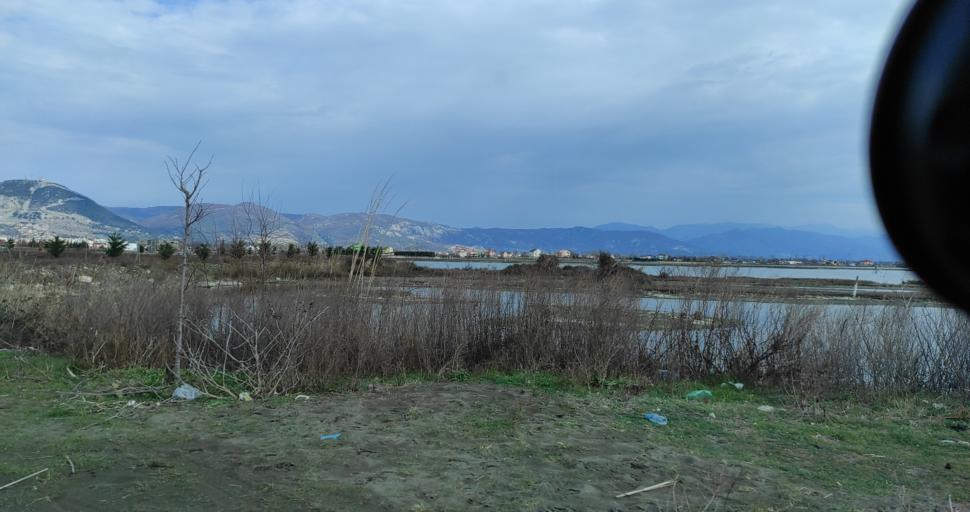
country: AL
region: Lezhe
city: Shengjin
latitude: 41.7706
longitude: 19.6007
